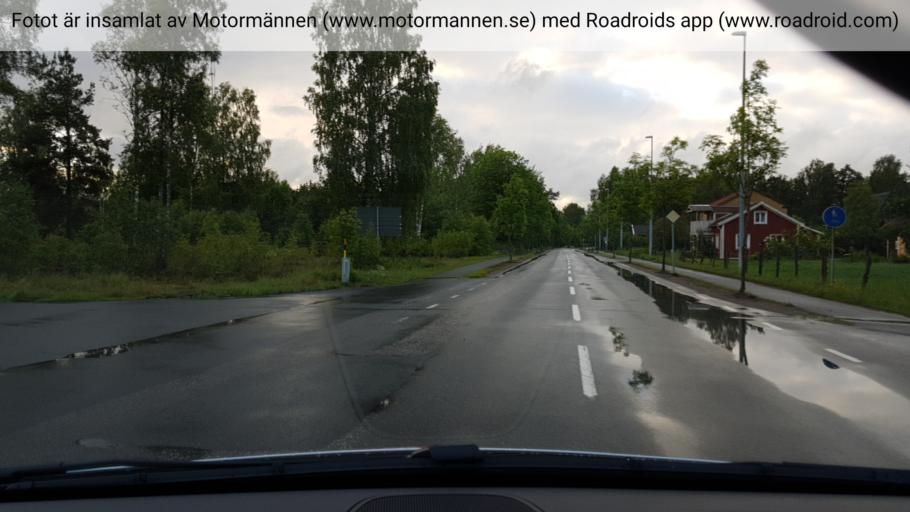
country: SE
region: Joenkoeping
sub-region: Vaggeryds Kommun
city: Skillingaryd
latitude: 57.3533
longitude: 14.0991
